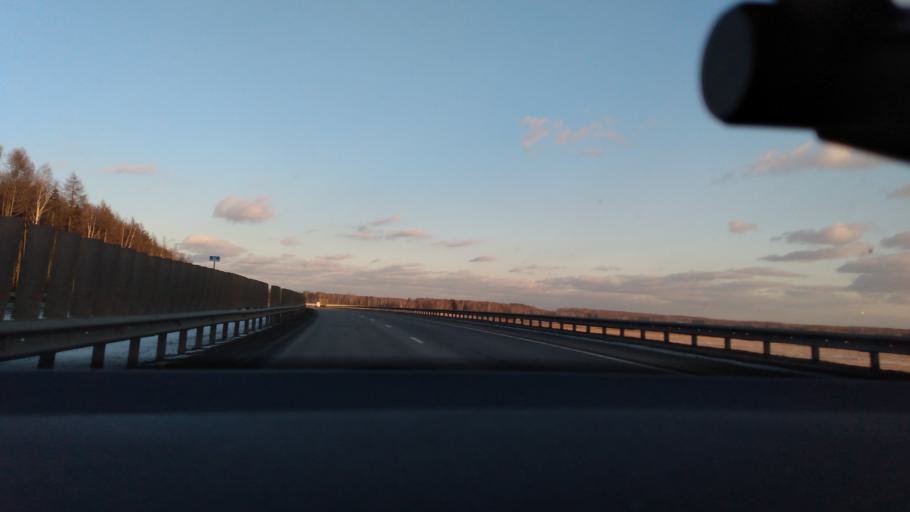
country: RU
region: Moskovskaya
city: Bronnitsy
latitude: 55.3814
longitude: 38.2684
